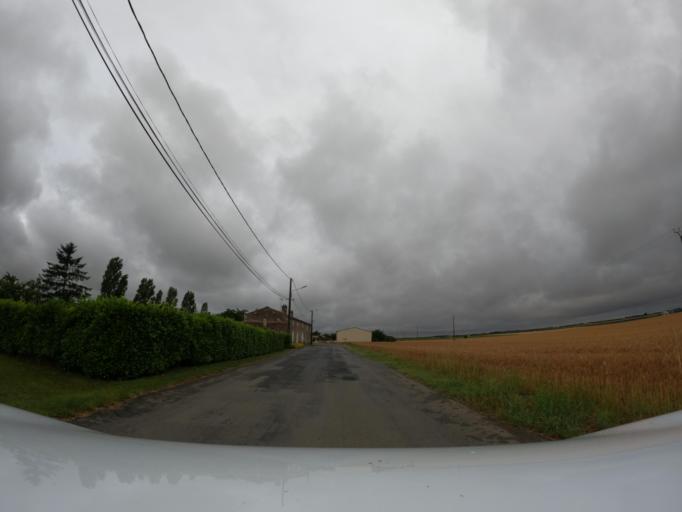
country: FR
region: Pays de la Loire
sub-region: Departement de la Vendee
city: Maillezais
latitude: 46.4051
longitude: -0.7340
